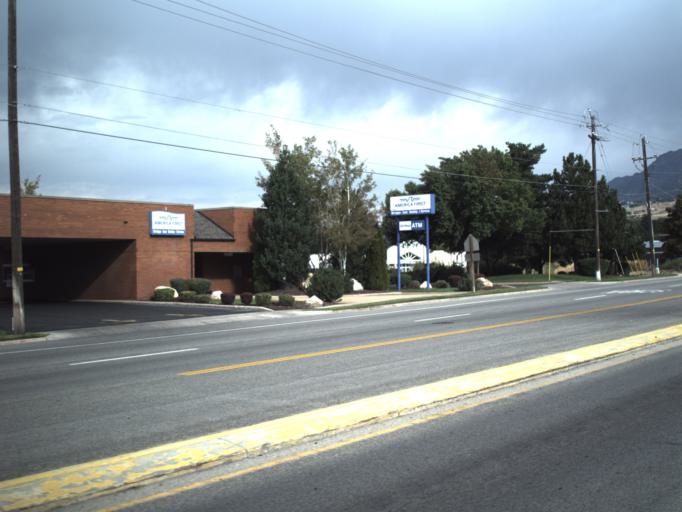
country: US
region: Utah
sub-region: Weber County
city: North Ogden
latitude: 41.3046
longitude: -111.9687
